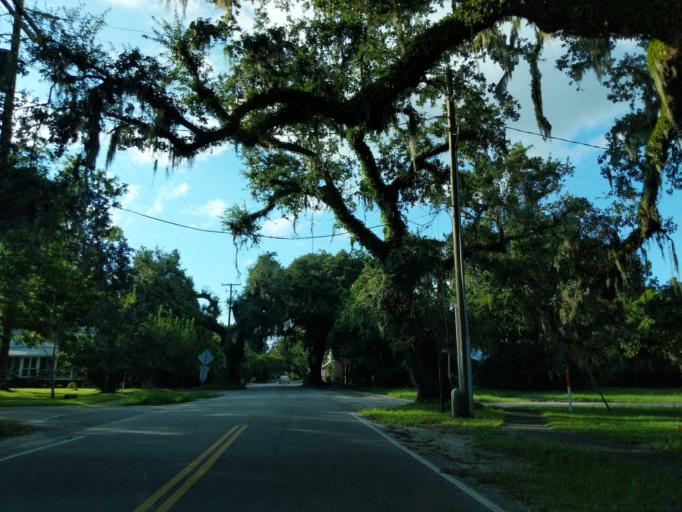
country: US
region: South Carolina
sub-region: Charleston County
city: Awendaw
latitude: 33.0892
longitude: -79.4620
